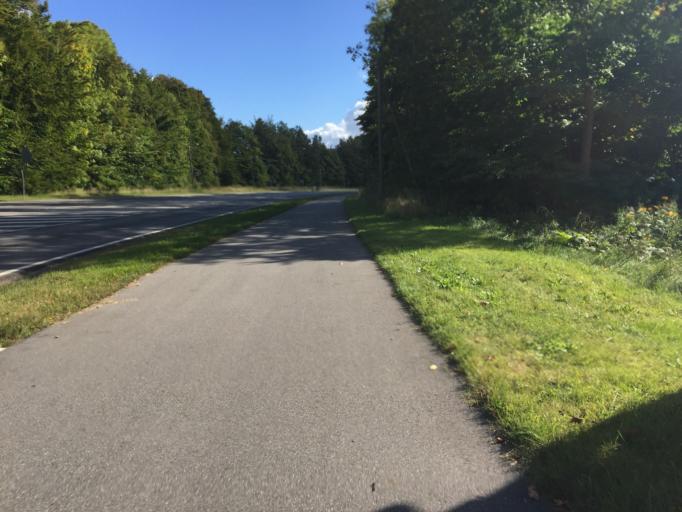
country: DK
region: Capital Region
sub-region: Fureso Kommune
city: Stavnsholt
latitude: 55.7718
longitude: 12.4257
